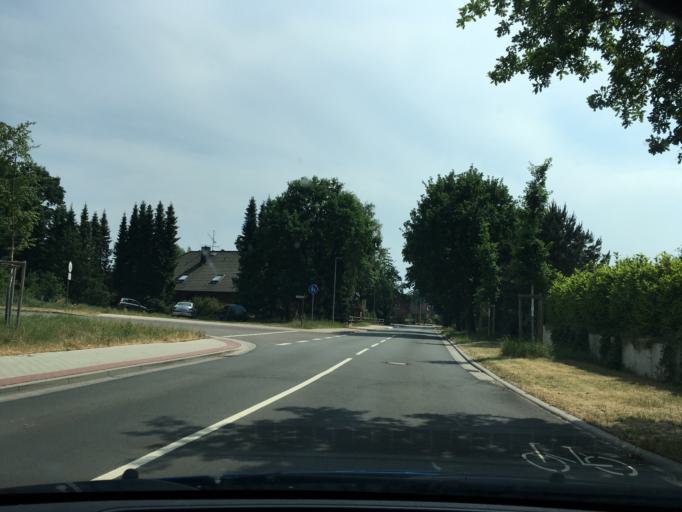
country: DE
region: Lower Saxony
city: Jesteburg
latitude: 53.2733
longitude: 9.9150
